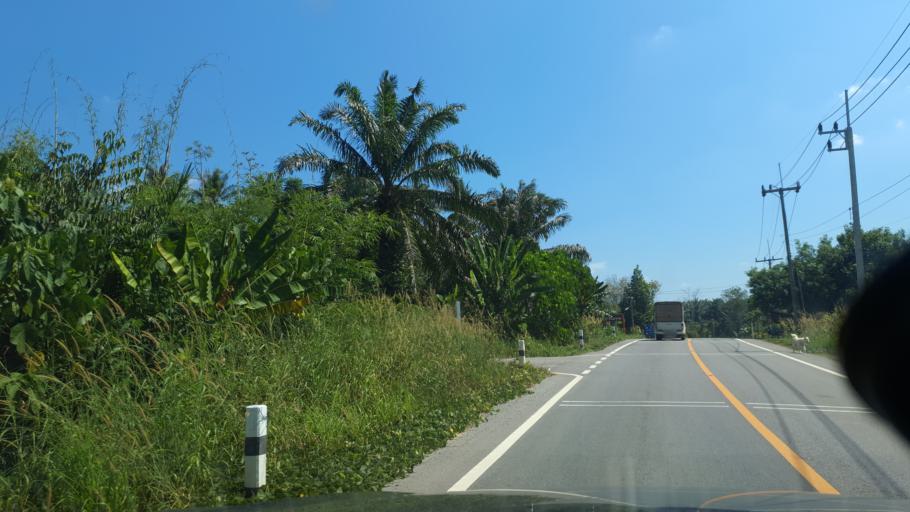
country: TH
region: Krabi
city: Khlong Thom
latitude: 7.9301
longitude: 99.2298
